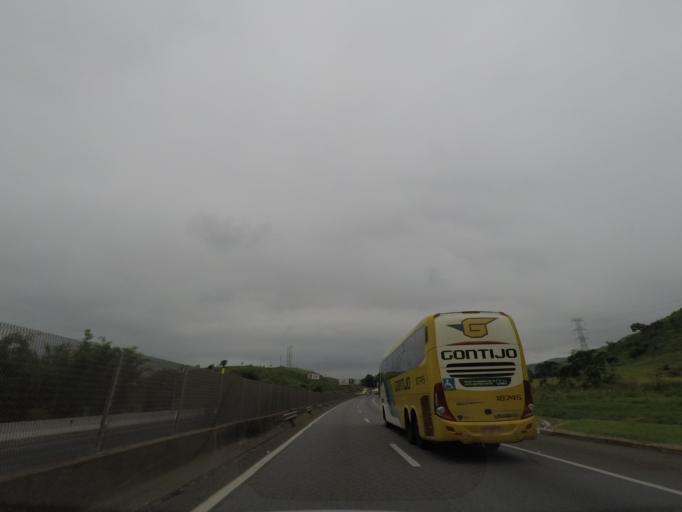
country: BR
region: Sao Paulo
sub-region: Aparecida
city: Aparecida
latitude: -22.8778
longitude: -45.2726
